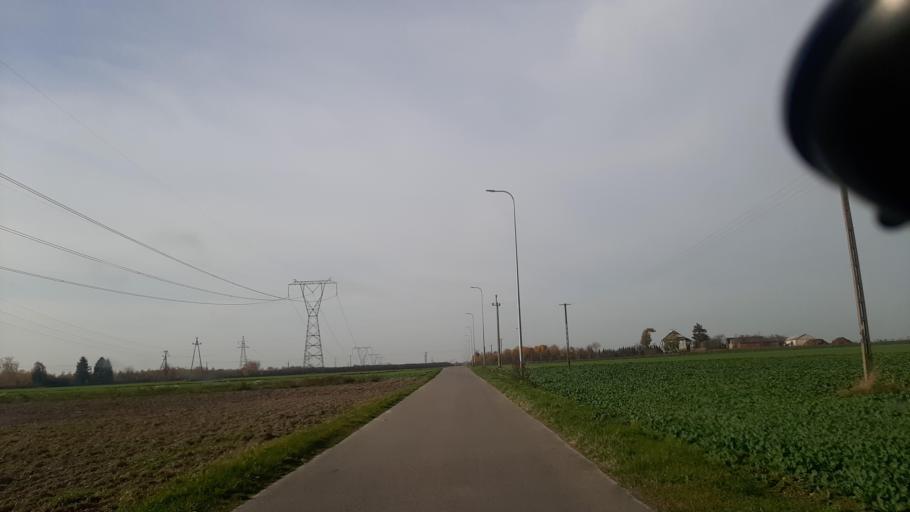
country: PL
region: Lublin Voivodeship
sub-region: Powiat lubelski
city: Lublin
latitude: 51.3331
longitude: 22.5353
